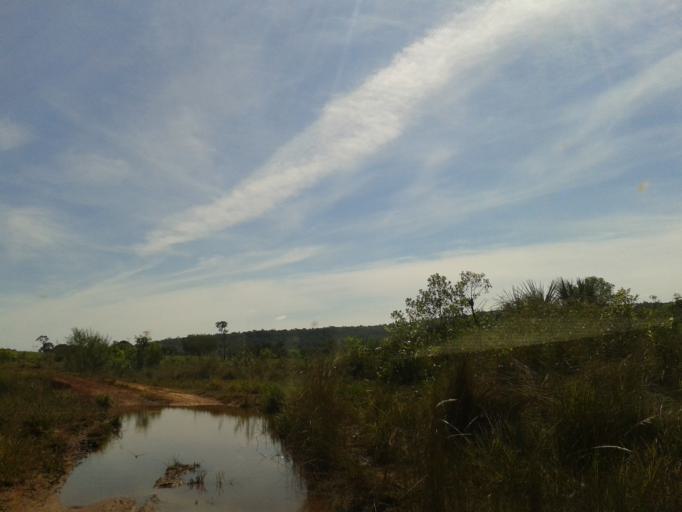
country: BR
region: Minas Gerais
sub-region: Campina Verde
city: Campina Verde
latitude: -19.4381
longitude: -49.6938
